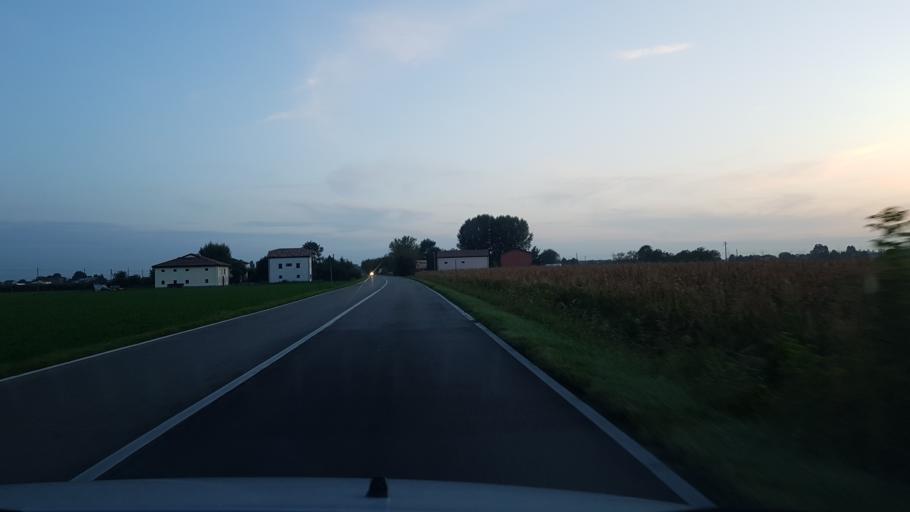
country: IT
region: Emilia-Romagna
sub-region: Provincia di Modena
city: Cavezzo
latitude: 44.8158
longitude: 11.0345
